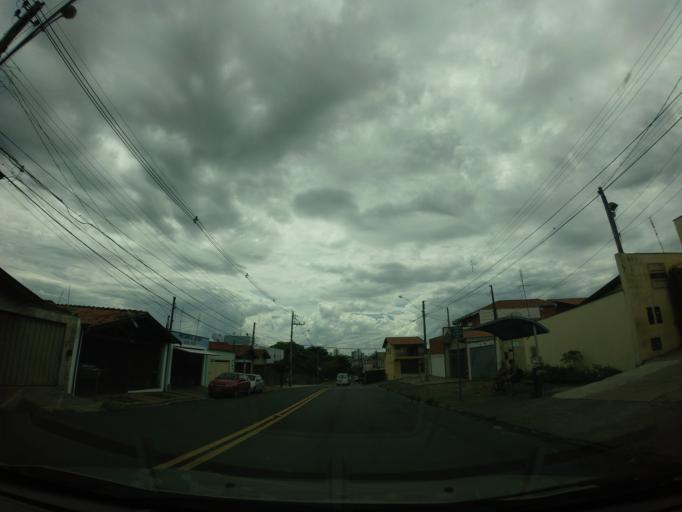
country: BR
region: Sao Paulo
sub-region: Piracicaba
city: Piracicaba
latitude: -22.7437
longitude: -47.6233
